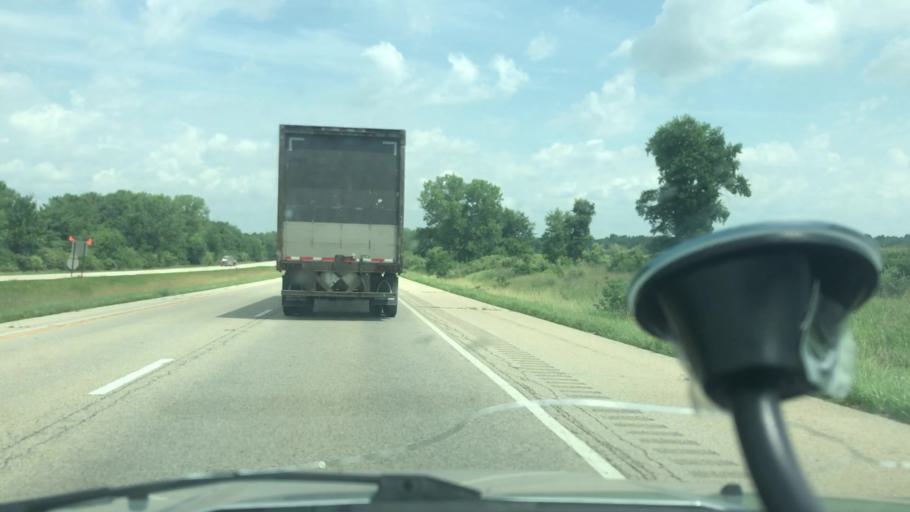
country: US
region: Illinois
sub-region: Peoria County
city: Bellevue
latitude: 40.7116
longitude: -89.6760
